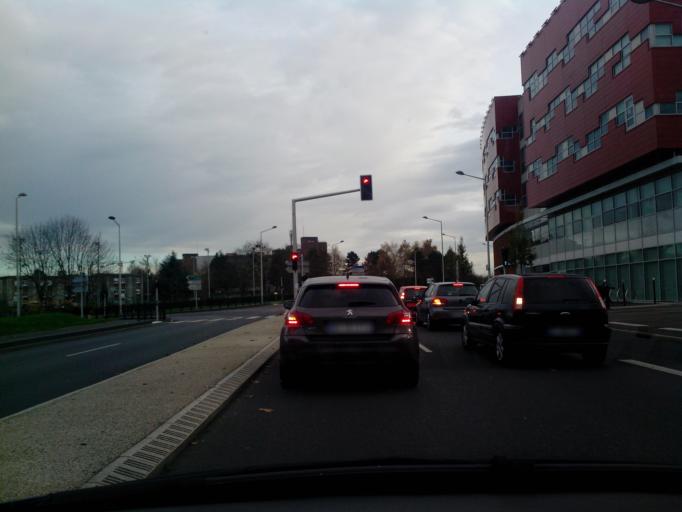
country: FR
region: Ile-de-France
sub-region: Departement de l'Essonne
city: Evry
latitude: 48.6263
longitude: 2.4398
